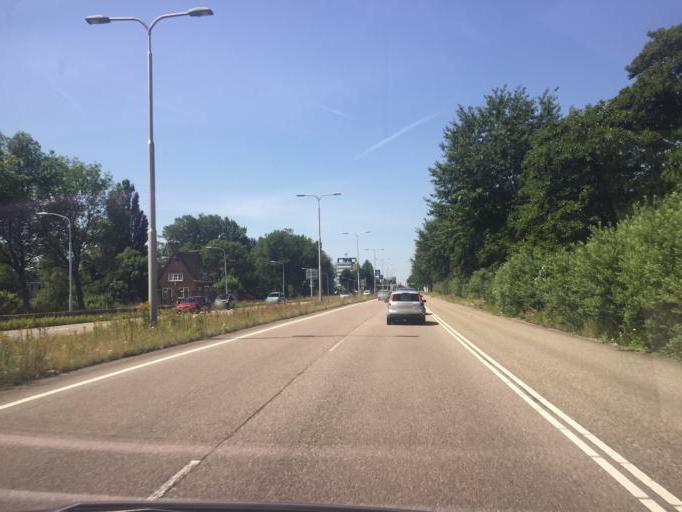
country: NL
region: North Holland
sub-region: Gemeente Haarlem
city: Haarlem
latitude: 52.3823
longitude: 4.6676
